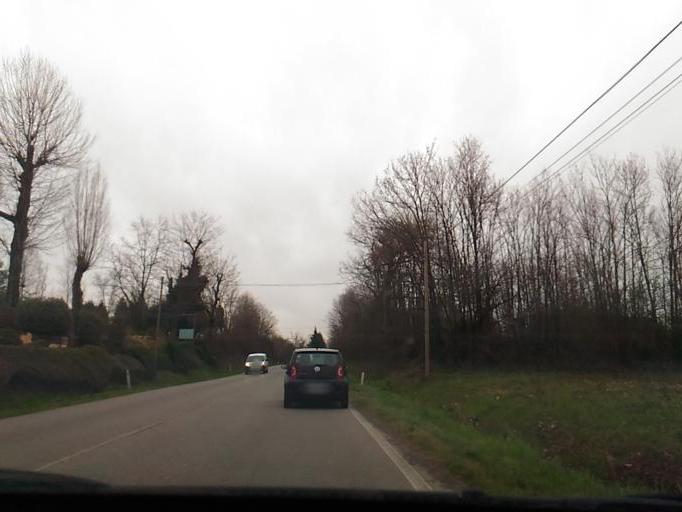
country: IT
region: Lombardy
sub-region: Provincia di Como
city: Figino Serenza
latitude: 45.7011
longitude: 9.1516
